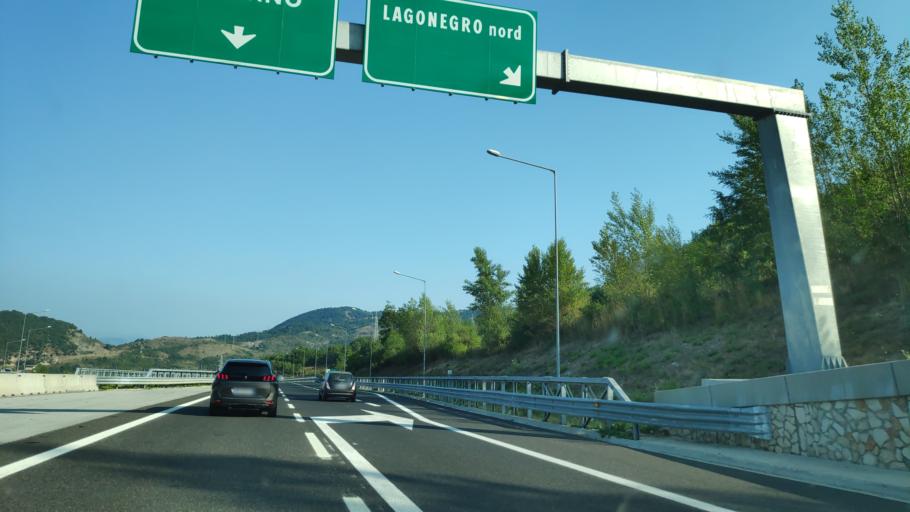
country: IT
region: Basilicate
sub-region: Provincia di Potenza
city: Lagonegro
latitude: 40.1498
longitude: 15.7508
